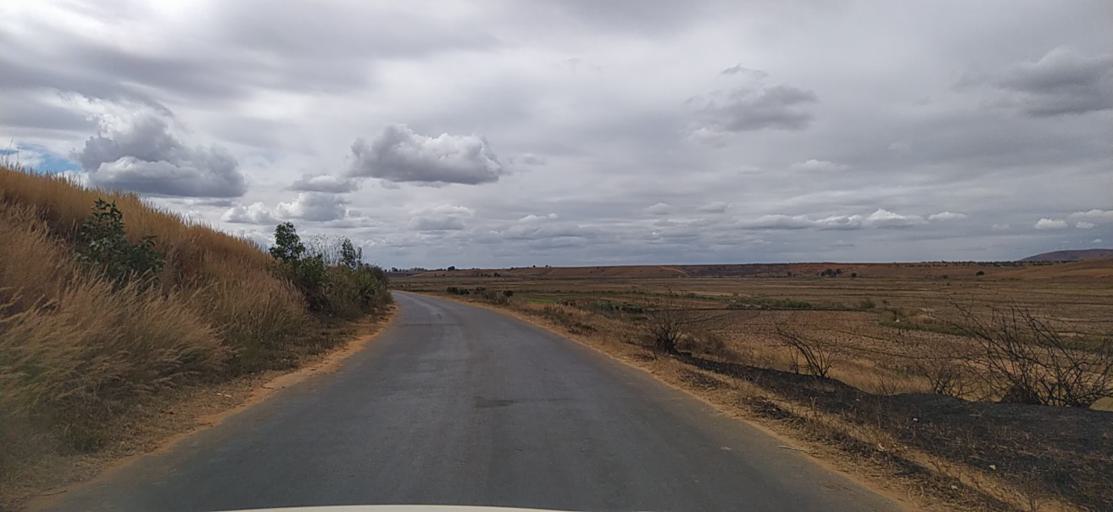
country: MG
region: Alaotra Mangoro
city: Ambatondrazaka
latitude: -17.9253
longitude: 48.2582
